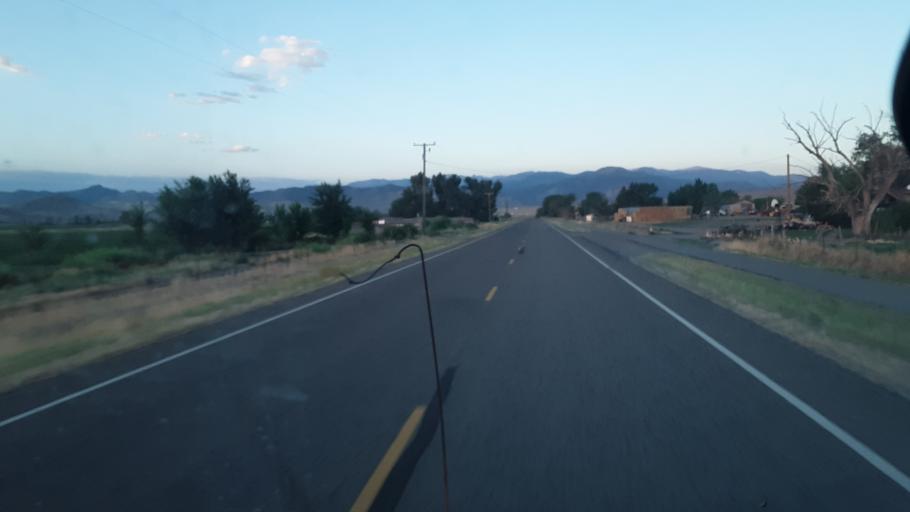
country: US
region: Utah
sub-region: Sevier County
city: Monroe
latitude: 38.6475
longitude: -112.2113
